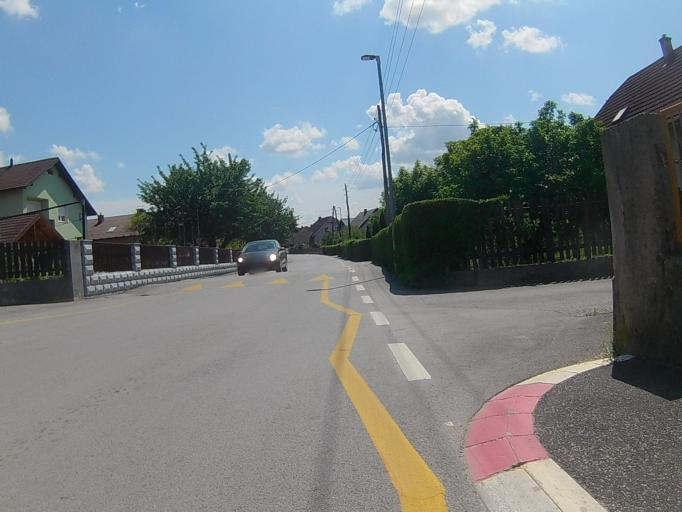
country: SI
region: Hoce-Slivnica
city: Rogoza
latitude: 46.4856
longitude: 15.6953
